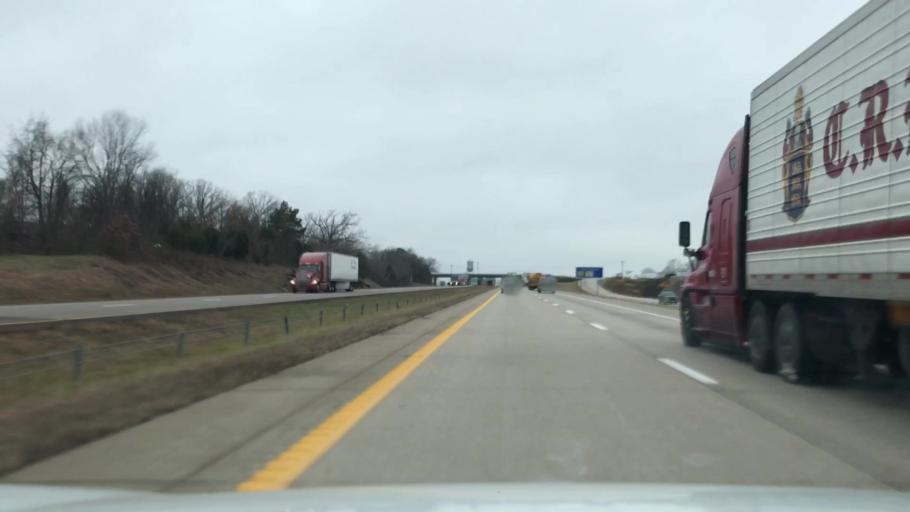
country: US
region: Missouri
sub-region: Crawford County
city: Bourbon
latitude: 38.1604
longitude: -91.2387
